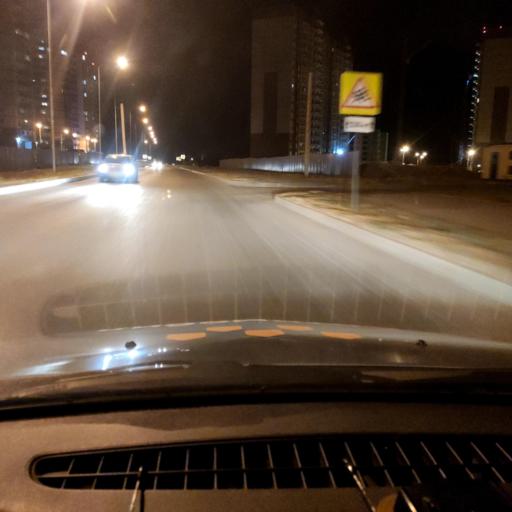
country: RU
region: Voronezj
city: Shilovo
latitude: 51.5689
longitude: 39.1218
